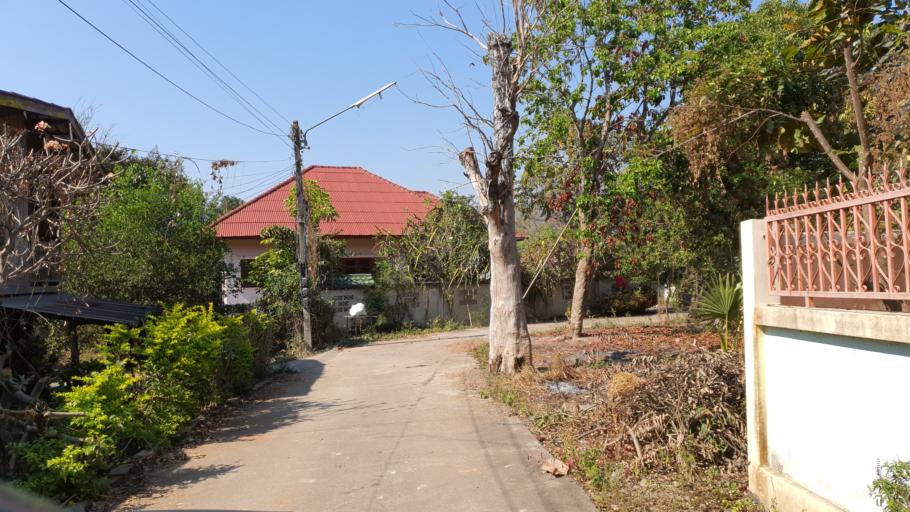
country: TH
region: Chiang Mai
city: Mae On
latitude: 18.7352
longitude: 99.2335
